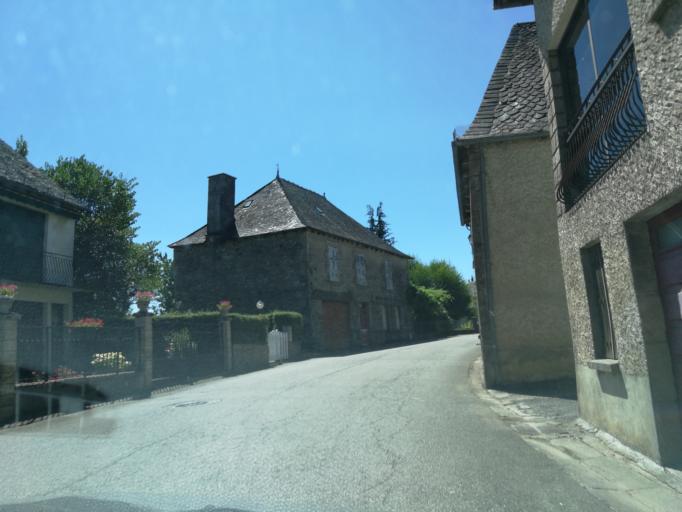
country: FR
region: Limousin
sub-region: Departement de la Correze
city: Argentat
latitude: 45.0403
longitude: 1.9539
